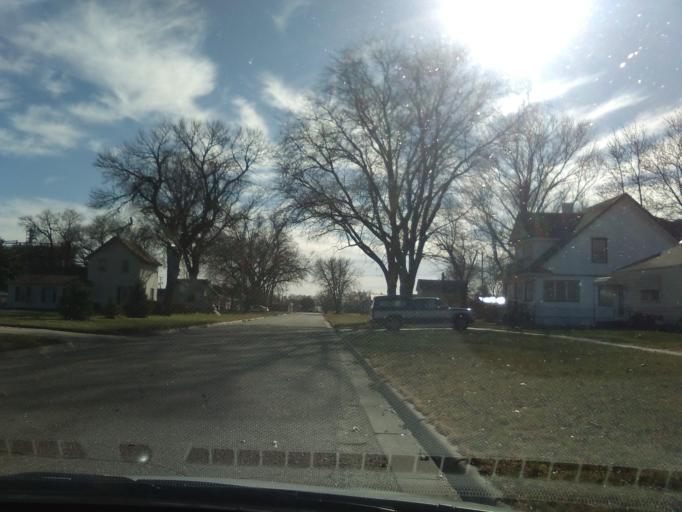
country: US
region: Nebraska
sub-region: Clay County
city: Harvard
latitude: 40.6207
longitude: -98.0986
